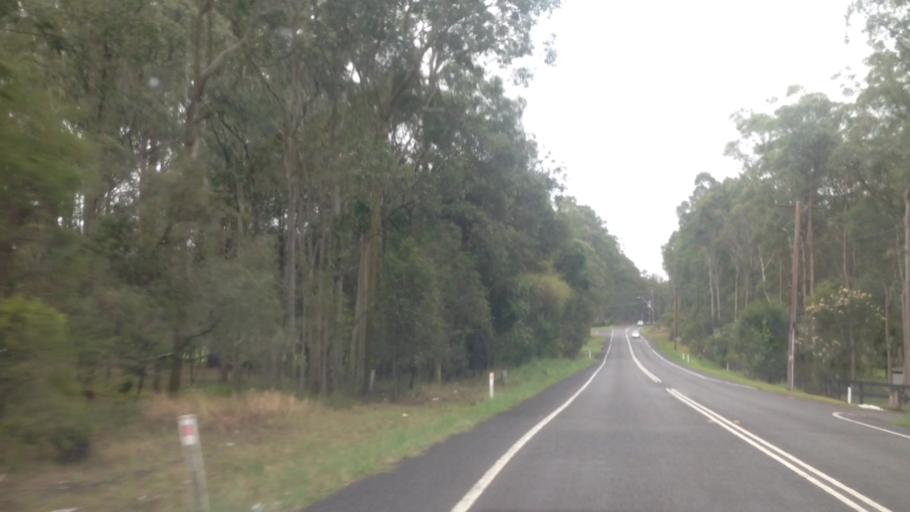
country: AU
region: New South Wales
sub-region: Wyong Shire
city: Little Jilliby
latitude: -33.2596
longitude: 151.3979
